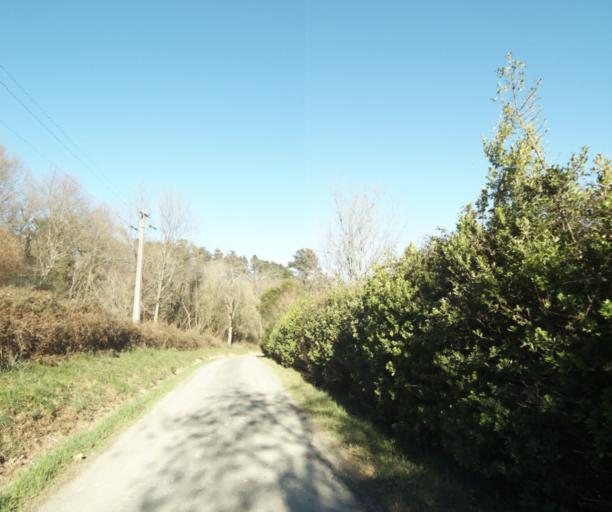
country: FR
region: Aquitaine
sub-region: Departement des Pyrenees-Atlantiques
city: Urrugne
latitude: 43.3616
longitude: -1.7343
